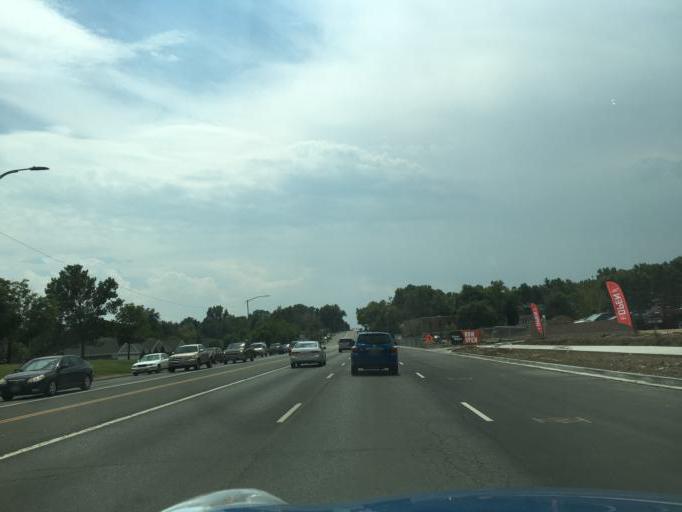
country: US
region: Colorado
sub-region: Jefferson County
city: Wheat Ridge
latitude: 39.7675
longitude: -105.0816
